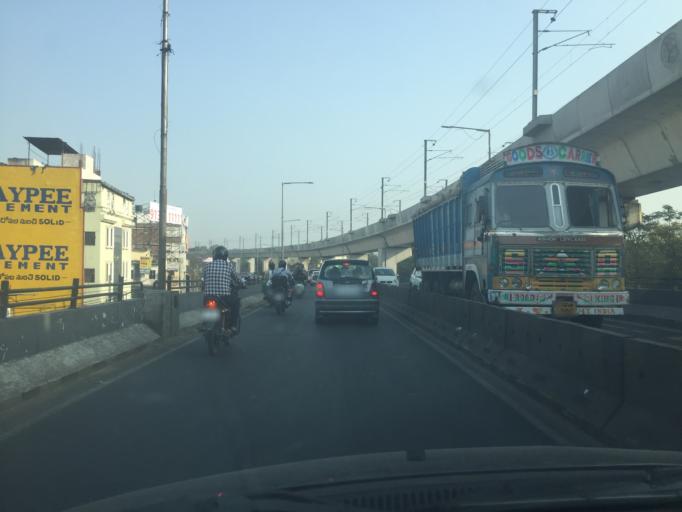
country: IN
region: Telangana
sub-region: Hyderabad
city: Malkajgiri
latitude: 17.4267
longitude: 78.5312
